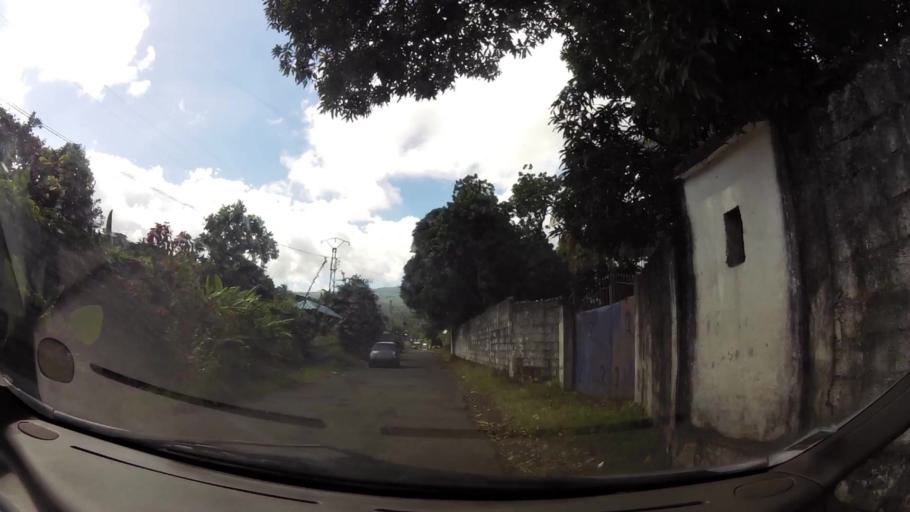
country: KM
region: Grande Comore
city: Mavingouni
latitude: -11.7397
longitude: 43.2473
